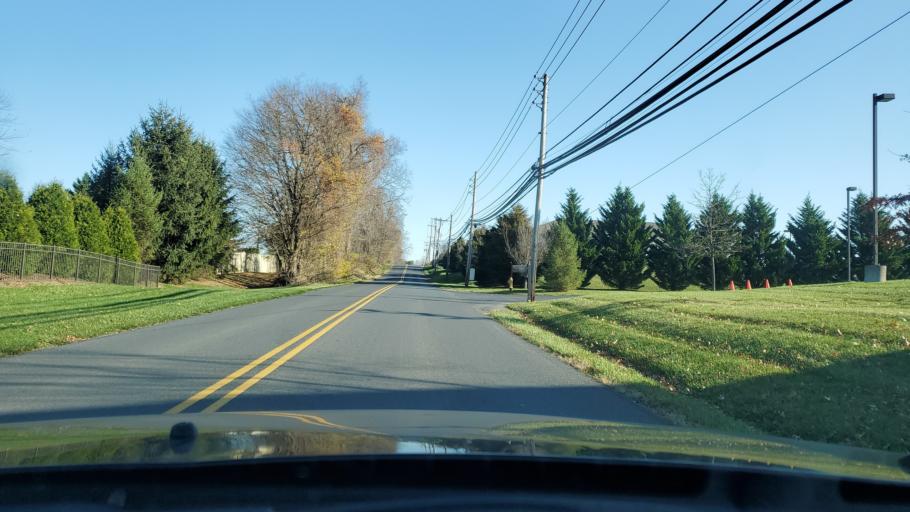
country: US
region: Pennsylvania
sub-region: Cumberland County
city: Mechanicsburg
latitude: 40.1675
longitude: -76.9990
